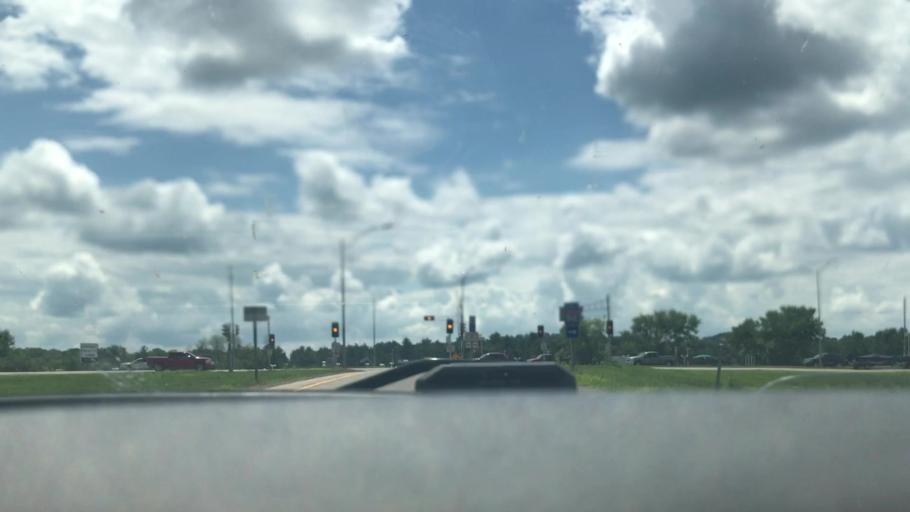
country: US
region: Wisconsin
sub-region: Jackson County
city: Black River Falls
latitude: 44.2962
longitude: -90.8248
